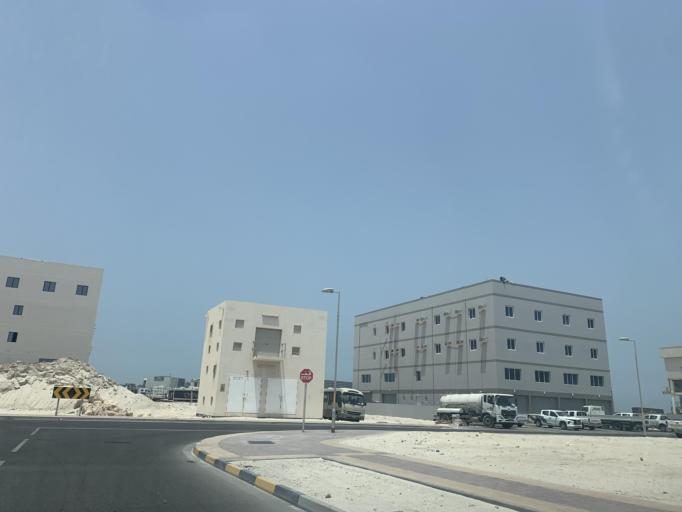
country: BH
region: Muharraq
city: Al Hadd
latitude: 26.2603
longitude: 50.6693
